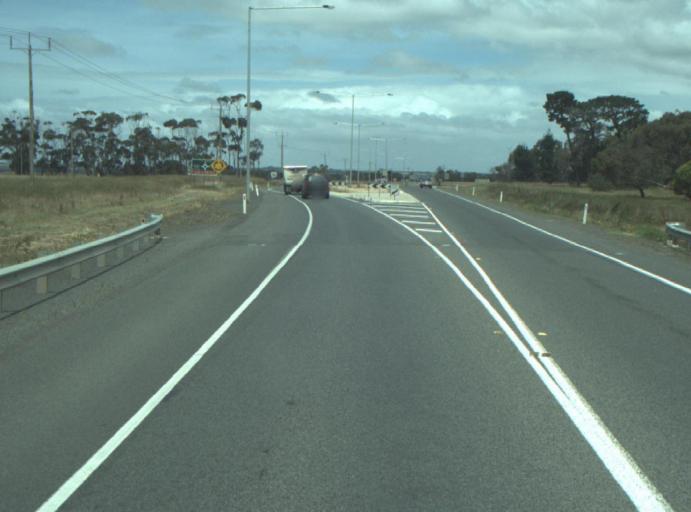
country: AU
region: Victoria
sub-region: Greater Geelong
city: Wandana Heights
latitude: -38.2393
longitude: 144.2786
